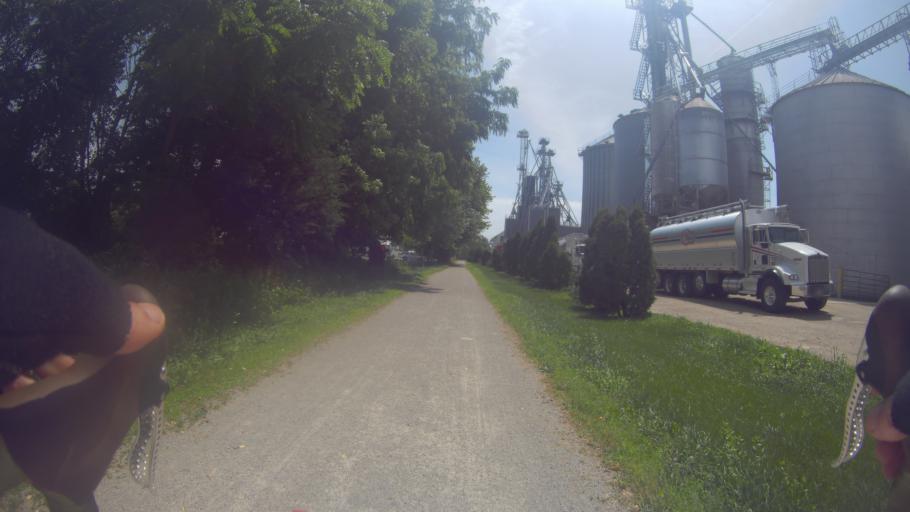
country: US
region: Wisconsin
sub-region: Jefferson County
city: Lake Mills
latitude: 43.0640
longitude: -88.9164
